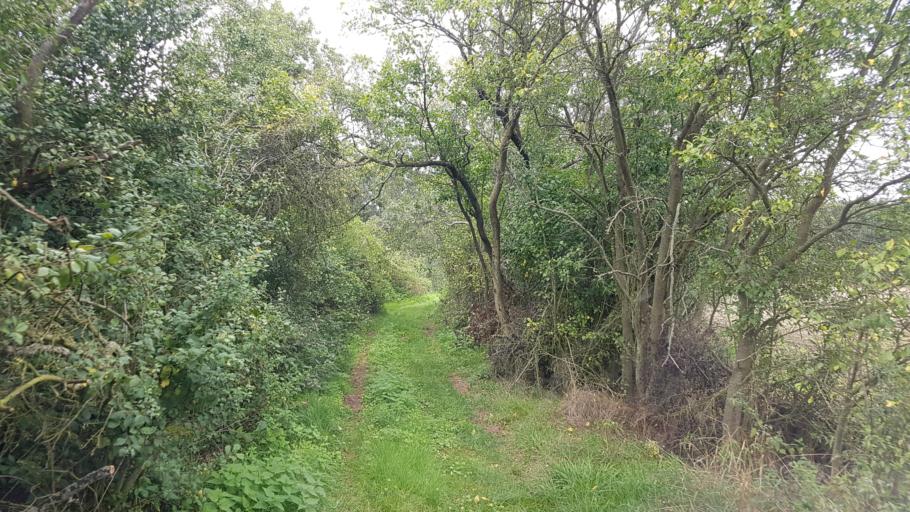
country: DE
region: Brandenburg
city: Hohenbucko
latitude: 51.6952
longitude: 13.4987
